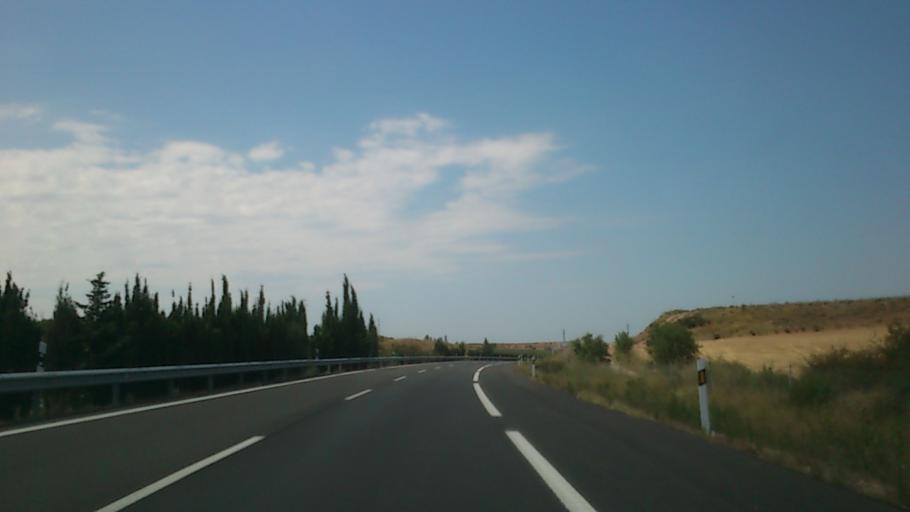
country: ES
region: La Rioja
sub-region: Provincia de La Rioja
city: Navarrete
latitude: 42.4493
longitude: -2.5703
